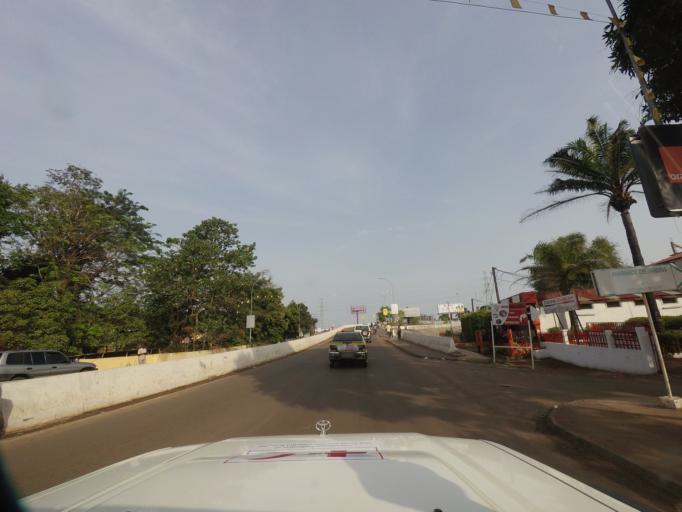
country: GN
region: Conakry
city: Camayenne
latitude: 9.5245
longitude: -13.6869
